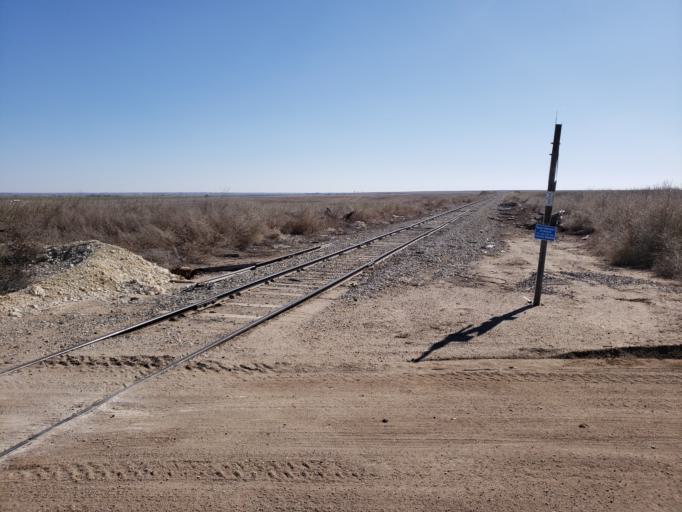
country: US
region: Kansas
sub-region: Ness County
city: Ness City
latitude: 38.4459
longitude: -100.0268
